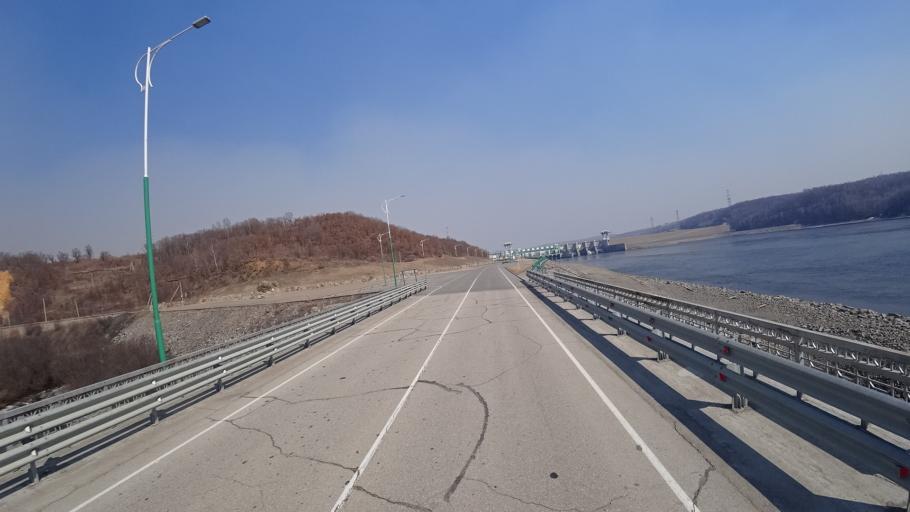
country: RU
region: Amur
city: Novobureyskiy
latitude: 49.7895
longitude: 129.9641
